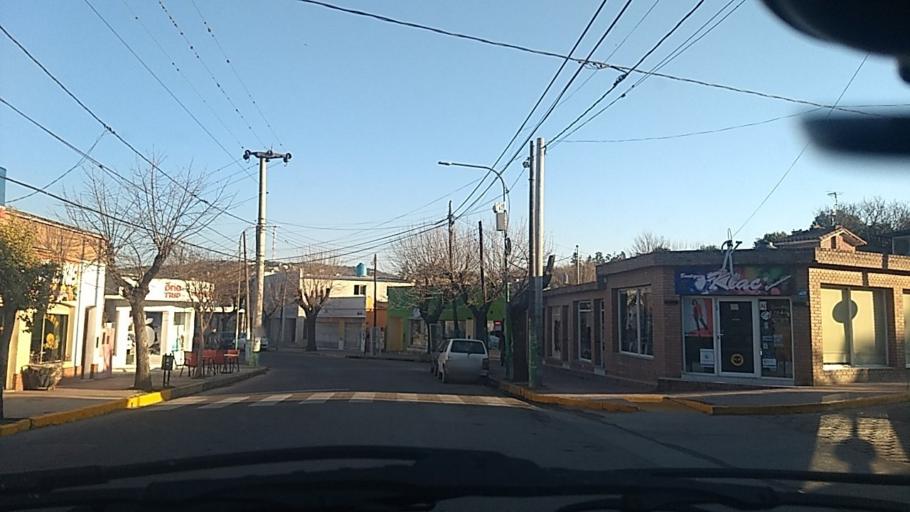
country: AR
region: Cordoba
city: Salsipuedes
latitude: -31.1377
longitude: -64.2928
